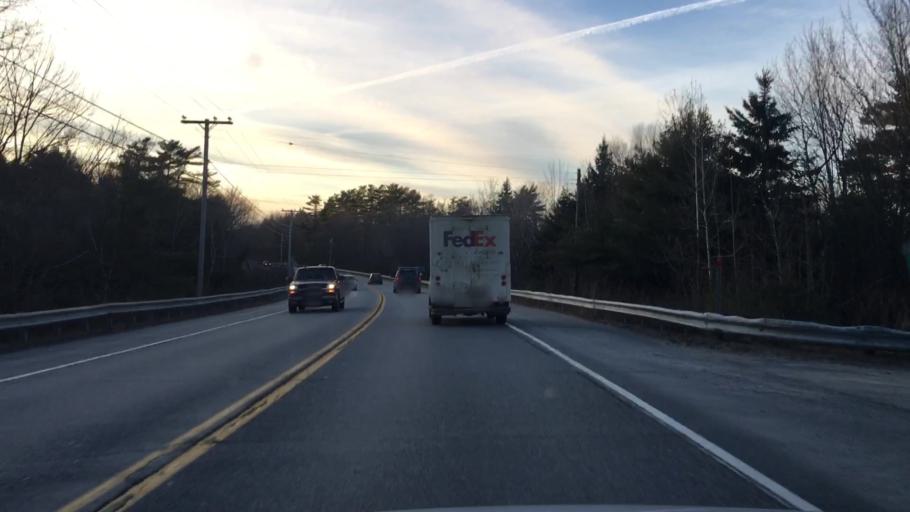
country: US
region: Maine
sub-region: Penobscot County
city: Holden
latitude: 44.7556
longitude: -68.6643
